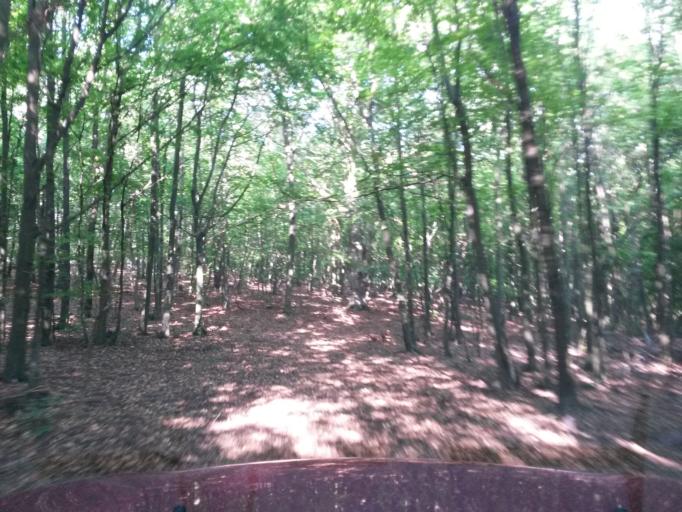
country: SK
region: Kosicky
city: Moldava nad Bodvou
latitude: 48.7276
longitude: 21.0810
